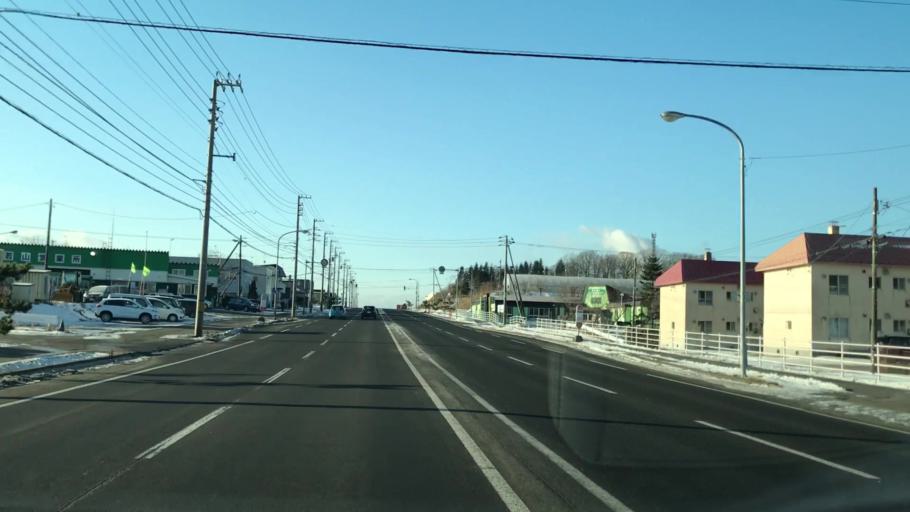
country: JP
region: Hokkaido
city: Muroran
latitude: 42.3907
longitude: 141.0770
